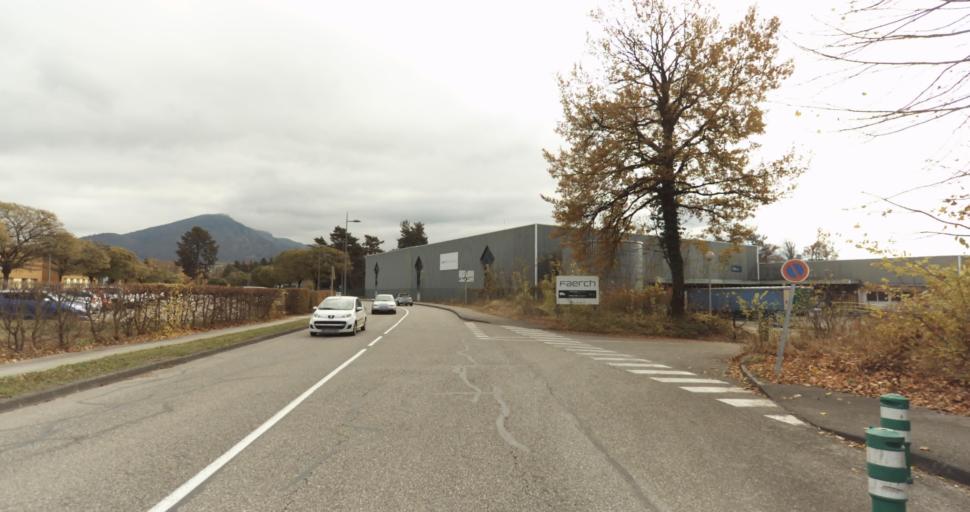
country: FR
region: Rhone-Alpes
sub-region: Departement de la Haute-Savoie
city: Metz-Tessy
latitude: 45.9302
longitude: 6.1143
